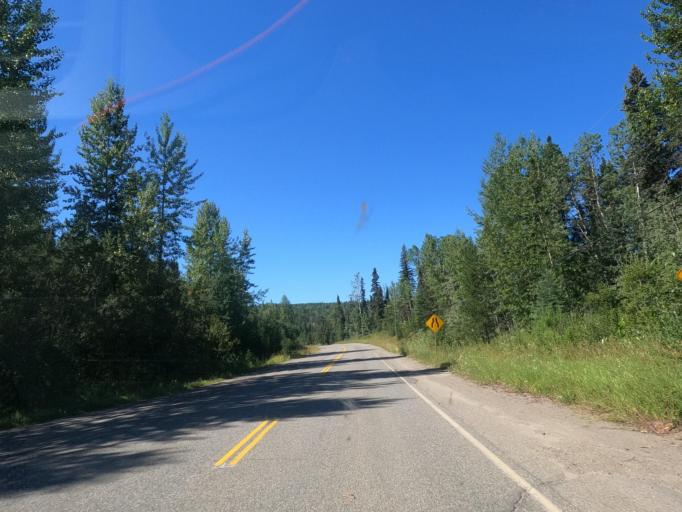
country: CA
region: British Columbia
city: Quesnel
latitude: 53.0536
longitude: -122.1782
